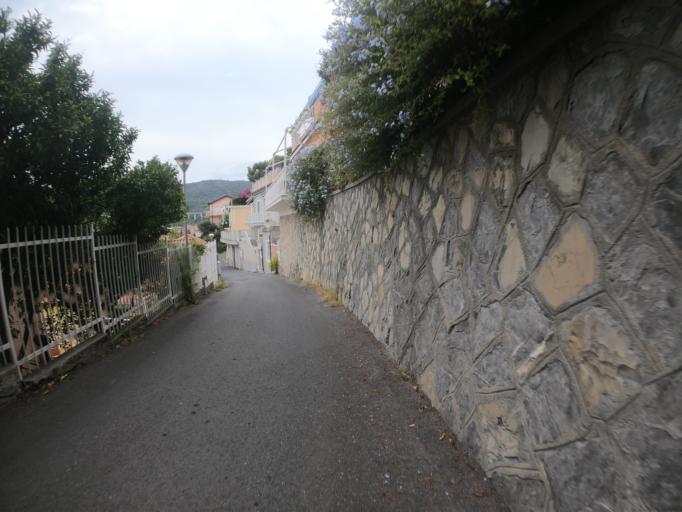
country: IT
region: Liguria
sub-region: Provincia di Savona
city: Marina di Andora
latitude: 43.9529
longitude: 8.1546
